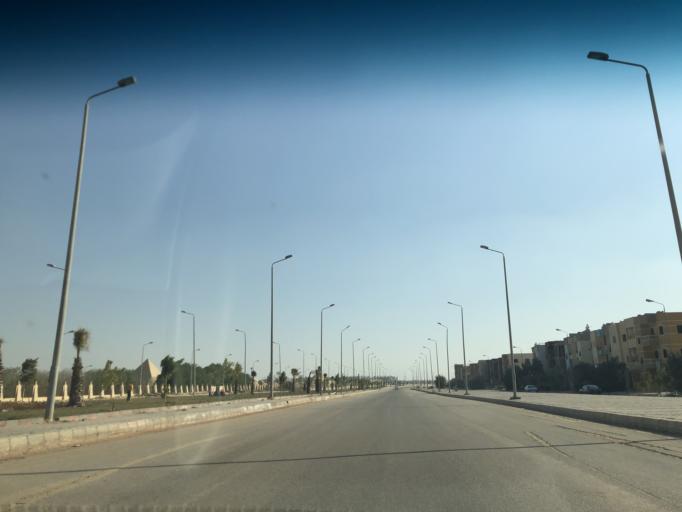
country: EG
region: Al Jizah
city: Madinat Sittah Uktubar
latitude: 29.9336
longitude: 31.0664
